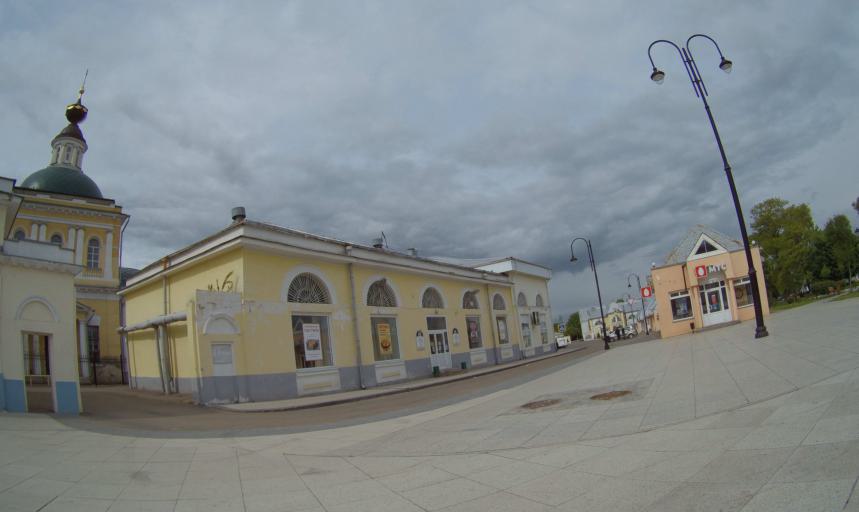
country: RU
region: Moskovskaya
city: Kolomna
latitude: 55.1017
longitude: 38.7560
